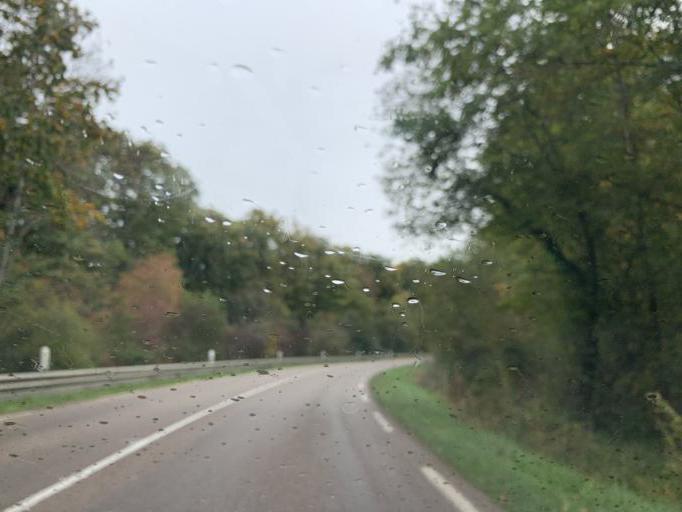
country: FR
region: Bourgogne
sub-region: Departement de l'Yonne
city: Moneteau
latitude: 47.8354
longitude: 3.5941
